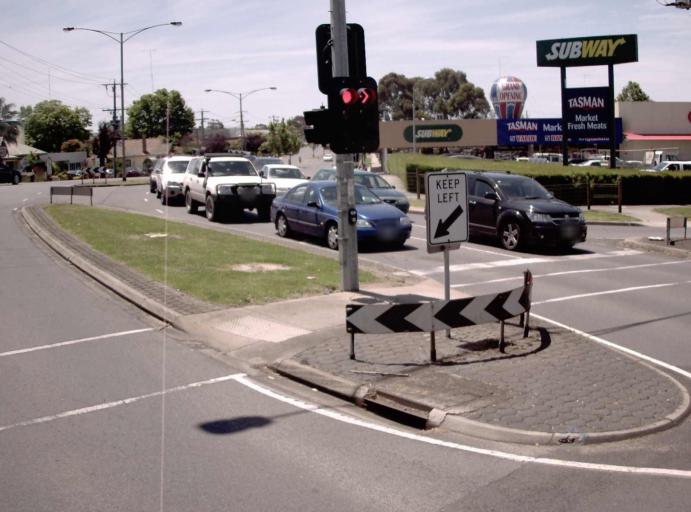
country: AU
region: Victoria
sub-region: Latrobe
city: Traralgon
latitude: -38.1995
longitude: 146.5329
